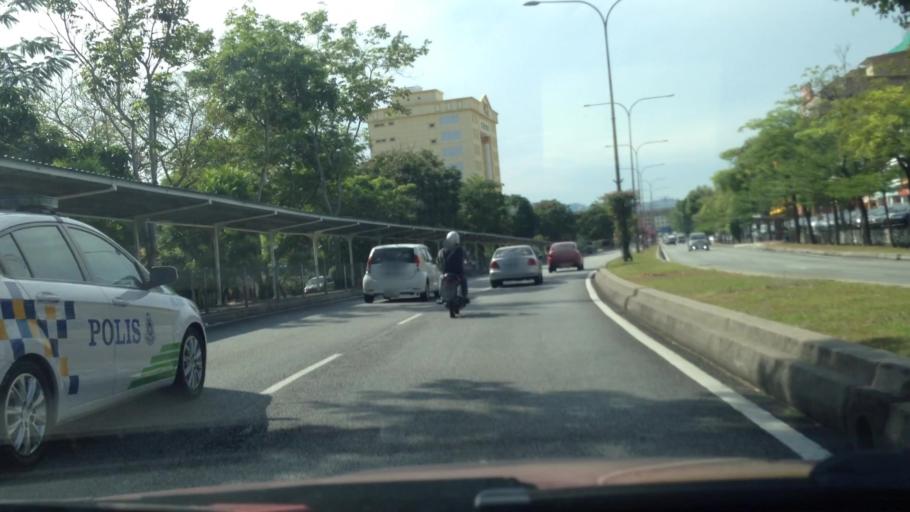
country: MY
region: Selangor
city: Subang Jaya
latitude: 3.0502
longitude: 101.5850
